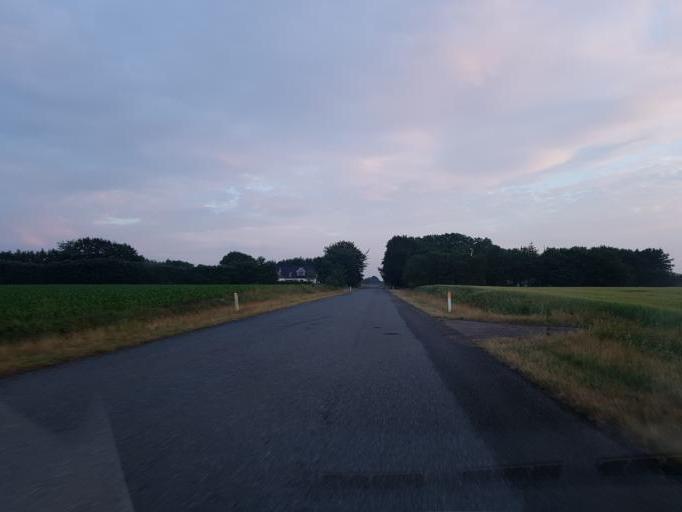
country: DK
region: South Denmark
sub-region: Esbjerg Kommune
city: Tjaereborg
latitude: 55.5191
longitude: 8.5711
